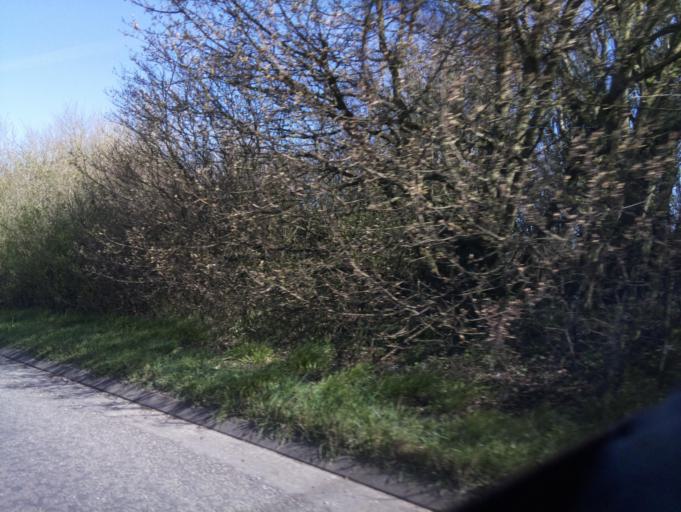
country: GB
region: England
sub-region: Wiltshire
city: Bradford-on-Avon
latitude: 51.3671
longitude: -2.2686
